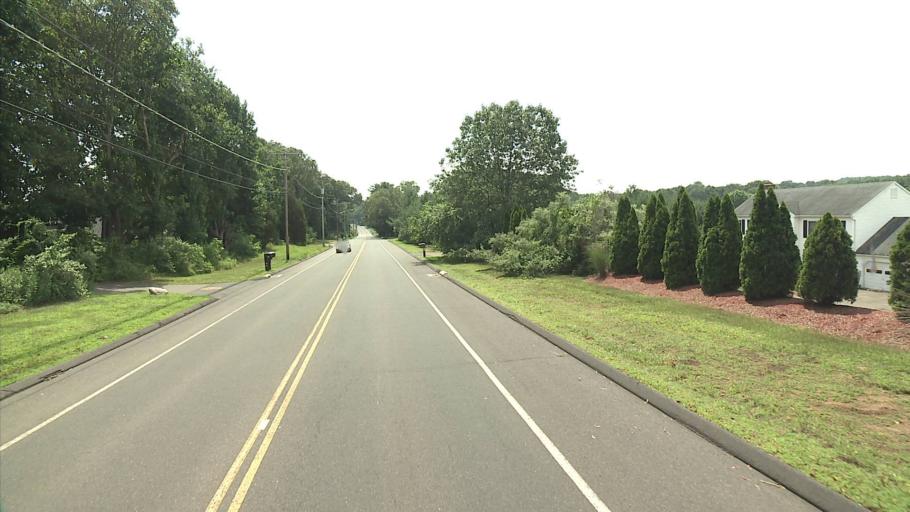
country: US
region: Connecticut
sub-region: New Haven County
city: Madison
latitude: 41.3082
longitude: -72.5925
